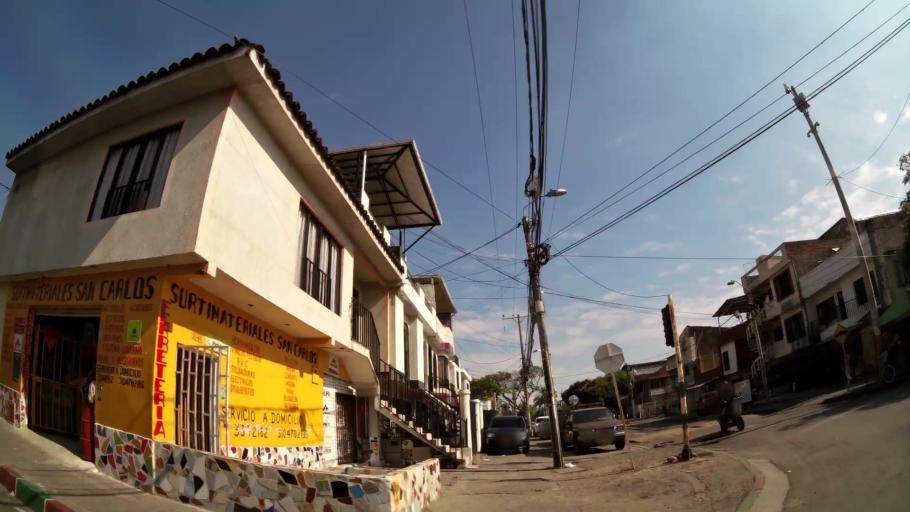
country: CO
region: Valle del Cauca
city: Cali
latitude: 3.4251
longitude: -76.5155
